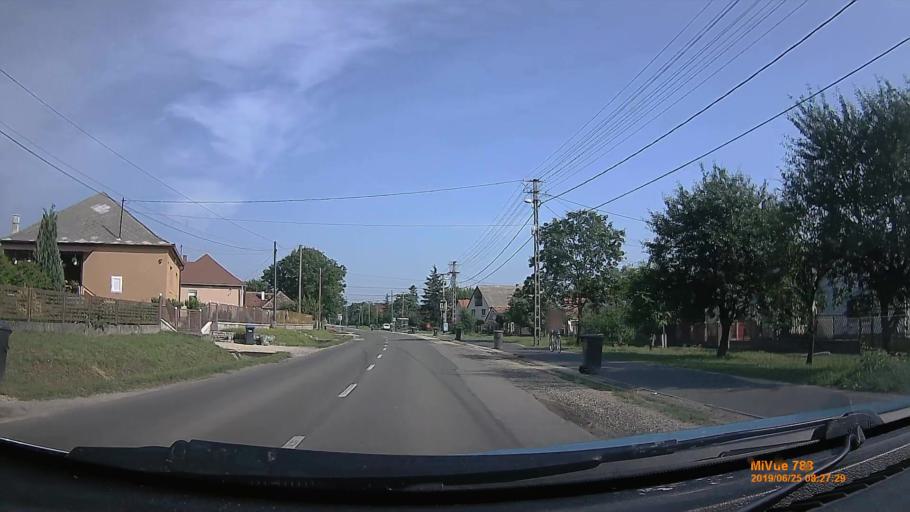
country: HU
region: Fejer
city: Szabadbattyan
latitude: 47.1131
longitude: 18.3800
